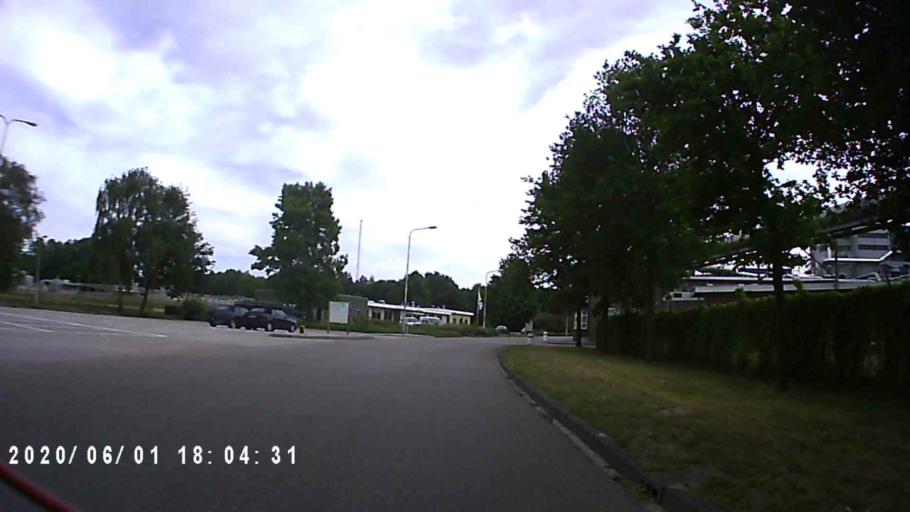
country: NL
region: Friesland
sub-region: Gemeente Tytsjerksteradiel
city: Sumar
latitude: 53.1824
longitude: 5.9939
